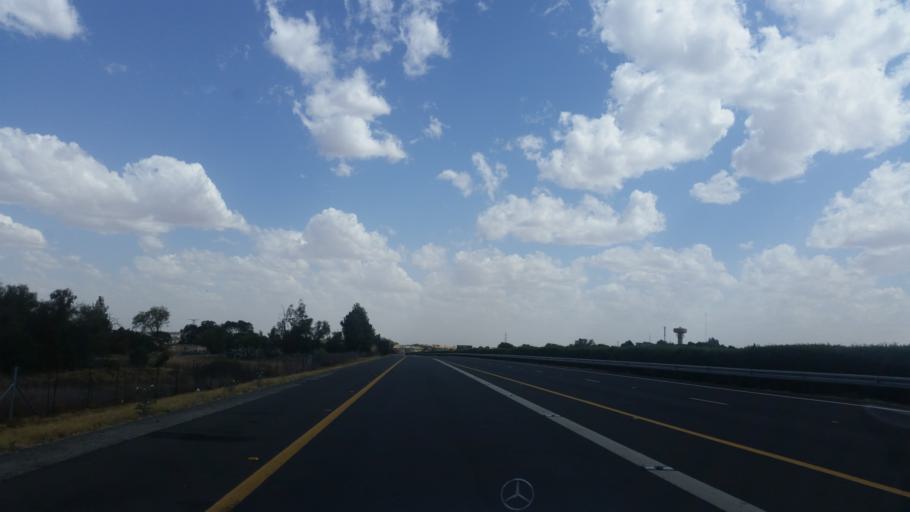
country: ZA
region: Orange Free State
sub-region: Mangaung Metropolitan Municipality
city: Bloemfontein
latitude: -29.0773
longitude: 26.1804
